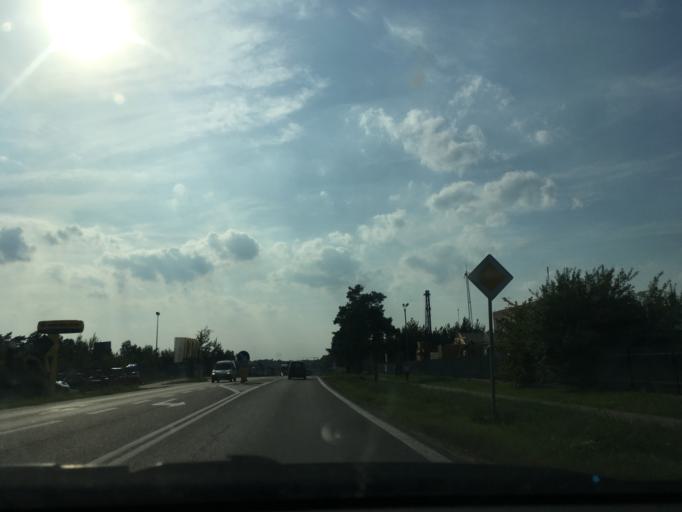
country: PL
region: Podlasie
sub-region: Bialystok
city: Bialystok
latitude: 53.1253
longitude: 23.2479
